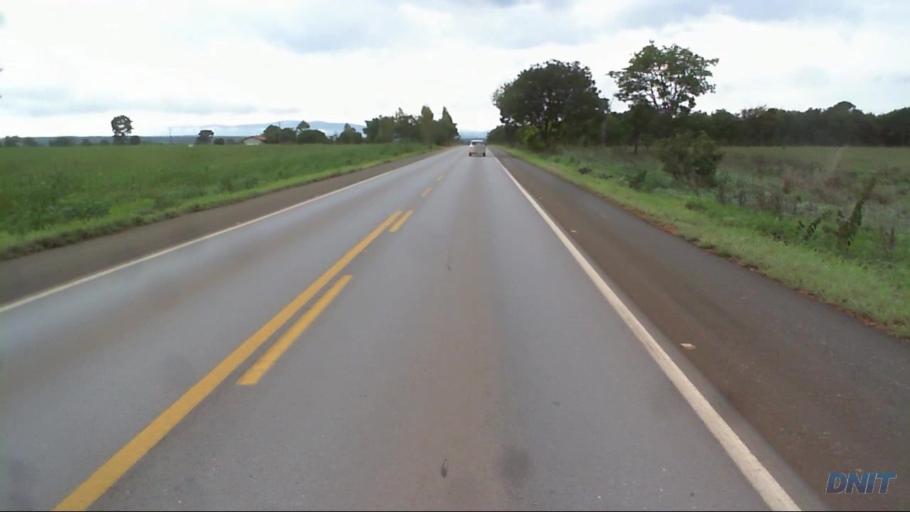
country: BR
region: Goias
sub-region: Uruacu
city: Uruacu
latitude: -14.7297
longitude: -49.0922
